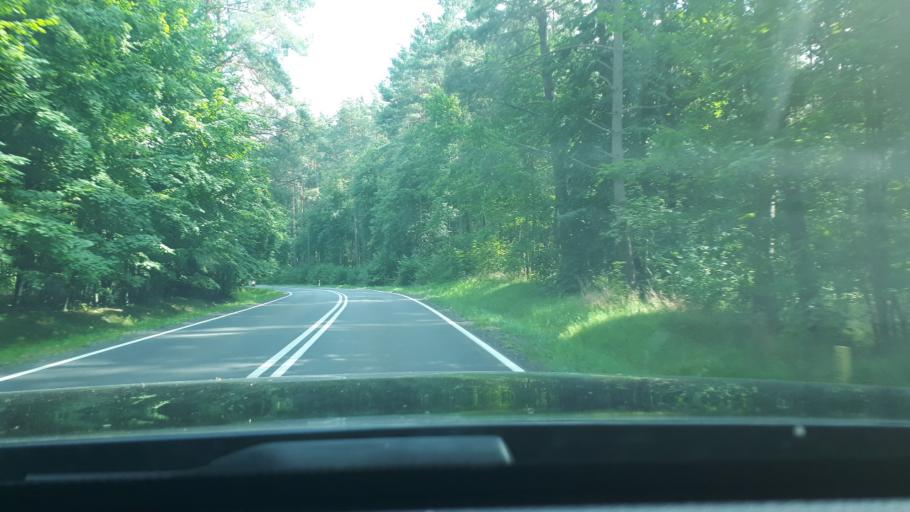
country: PL
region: Warmian-Masurian Voivodeship
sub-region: Powiat olsztynski
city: Stawiguda
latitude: 53.5416
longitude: 20.4209
